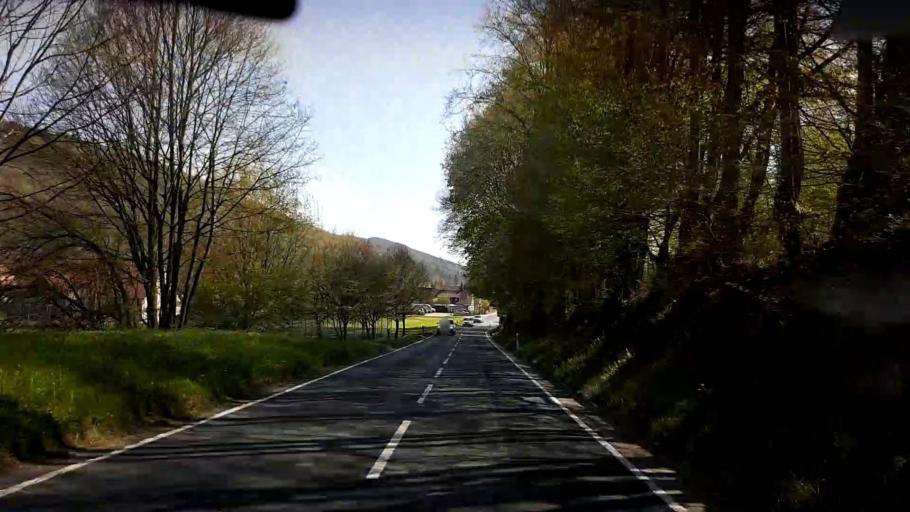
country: DE
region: Bavaria
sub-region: Upper Franconia
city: Unterleinleiter
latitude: 49.8258
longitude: 11.1894
